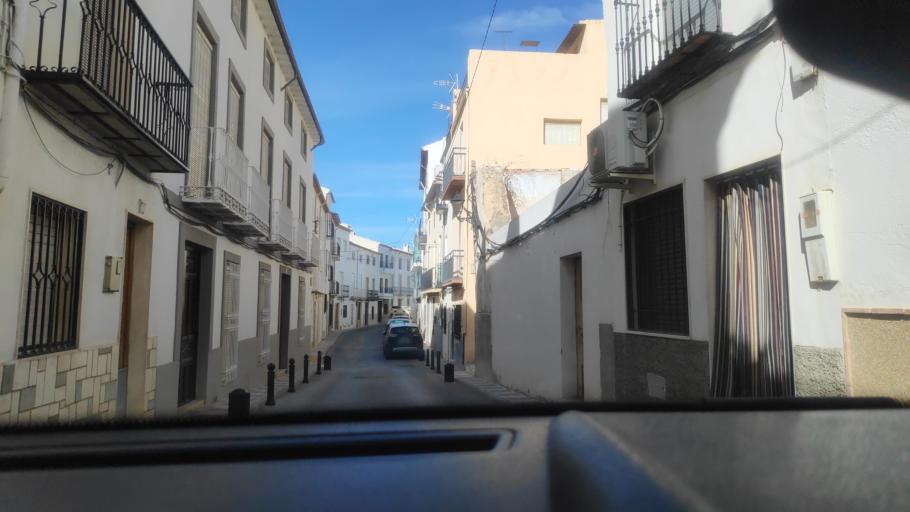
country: ES
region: Andalusia
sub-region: Provincia de Jaen
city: Torres
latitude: 37.7841
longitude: -3.5067
